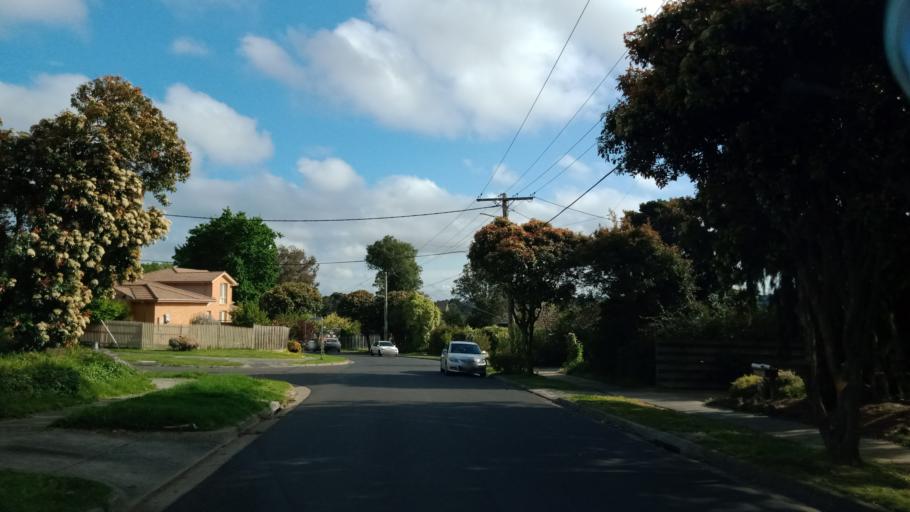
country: AU
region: Victoria
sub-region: Monash
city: Notting Hill
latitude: -37.8896
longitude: 145.1516
